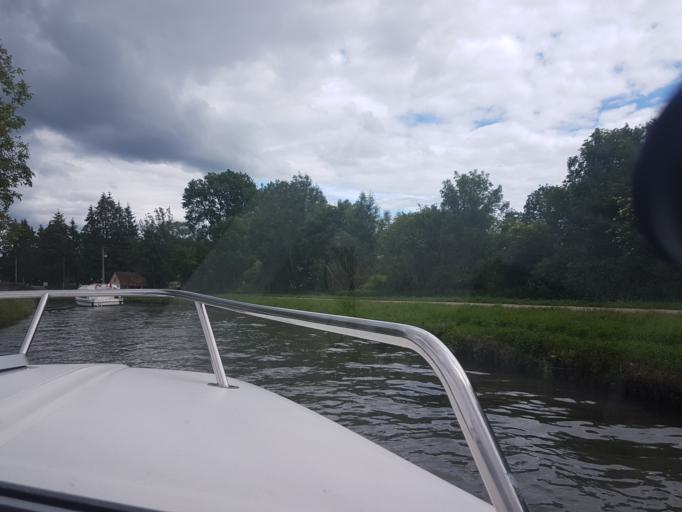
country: FR
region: Bourgogne
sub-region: Departement de l'Yonne
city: Vermenton
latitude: 47.5669
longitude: 3.6389
